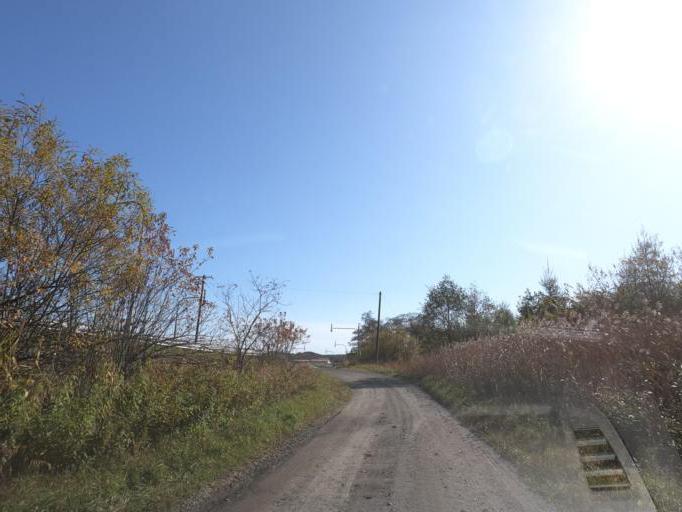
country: JP
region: Hokkaido
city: Obihiro
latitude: 42.7269
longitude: 143.4550
